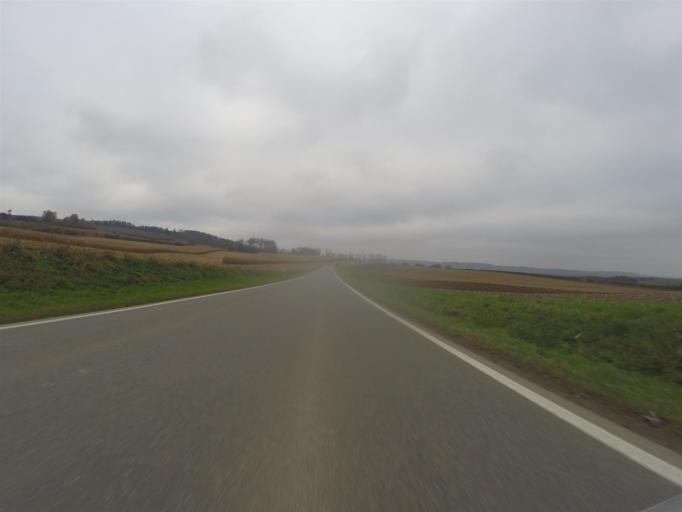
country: DE
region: Thuringia
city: Schongleina
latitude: 50.9140
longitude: 11.7312
